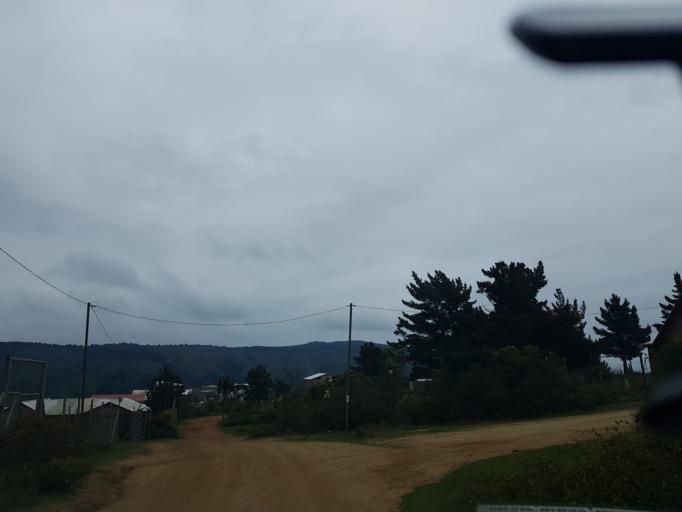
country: CL
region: Valparaiso
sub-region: Provincia de Valparaiso
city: Valparaiso
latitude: -33.1366
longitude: -71.6582
